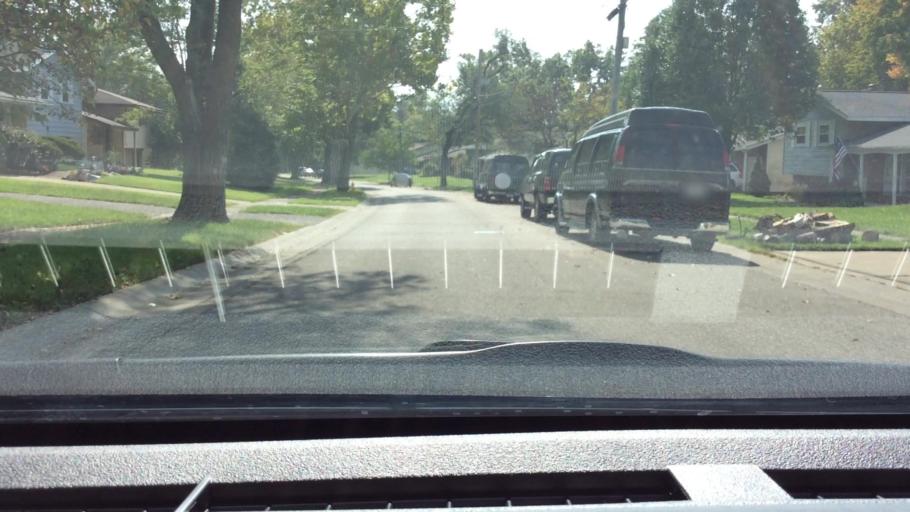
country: US
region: Ohio
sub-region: Hamilton County
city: Greenhills
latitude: 39.2701
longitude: -84.5041
